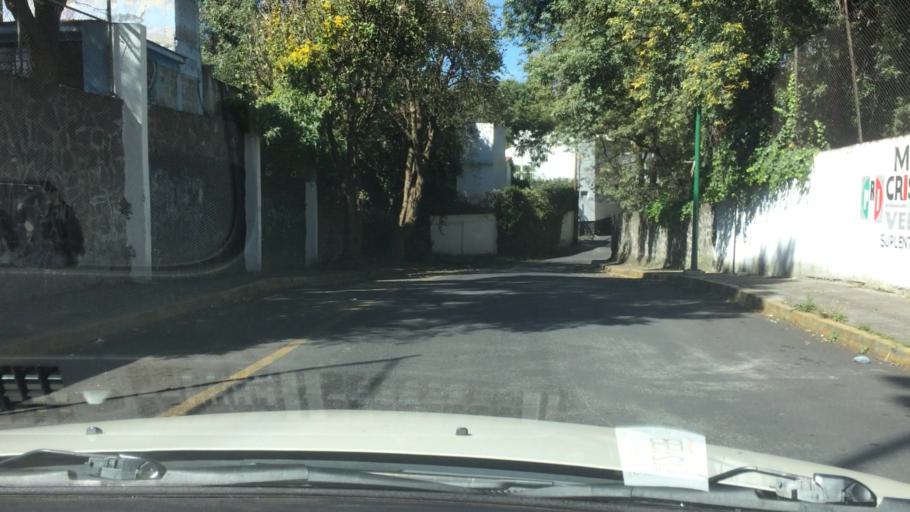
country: MX
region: Mexico City
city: Magdalena Contreras
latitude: 19.3238
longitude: -99.2207
